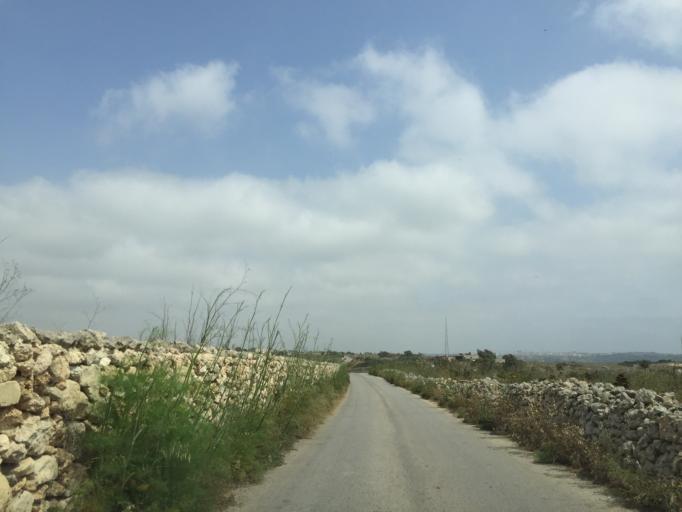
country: MT
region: L-Imgarr
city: Imgarr
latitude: 35.8973
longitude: 14.3557
